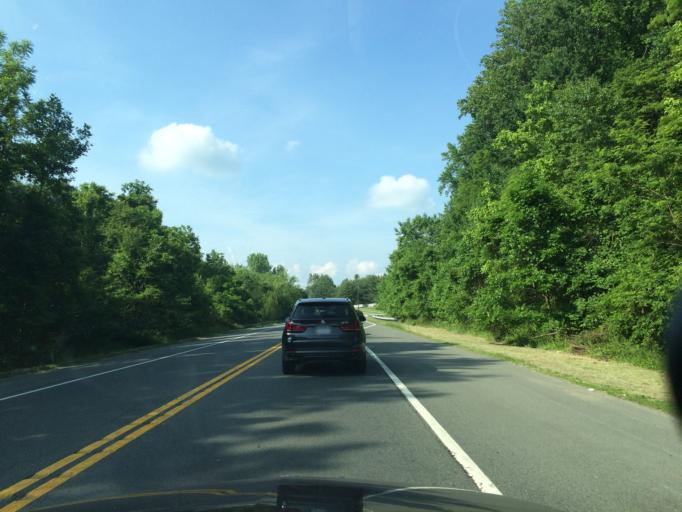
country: US
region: Maryland
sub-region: Montgomery County
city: Olney
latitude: 39.1636
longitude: -77.0615
